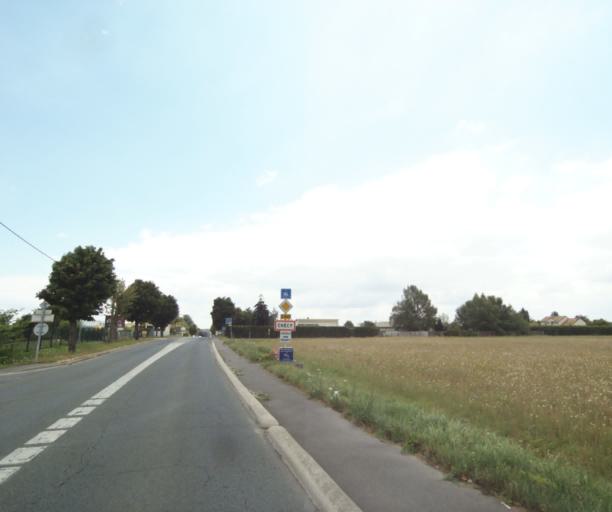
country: FR
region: Centre
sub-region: Departement du Loiret
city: Checy
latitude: 47.9016
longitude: 2.0052
